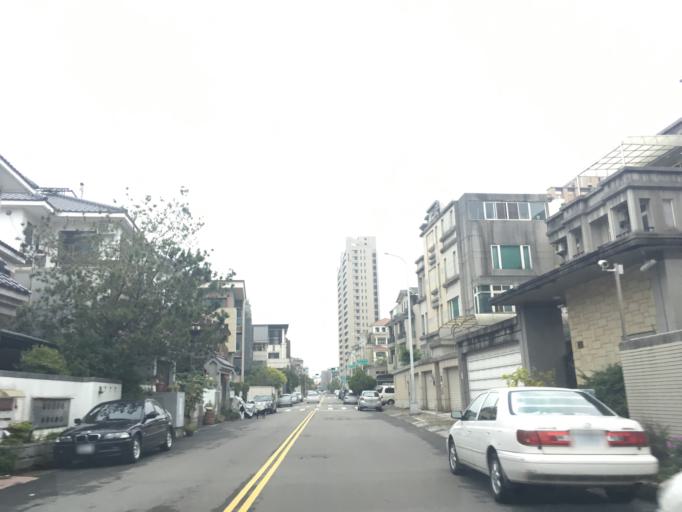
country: TW
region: Taiwan
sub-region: Taichung City
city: Taichung
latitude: 24.1690
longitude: 120.7169
